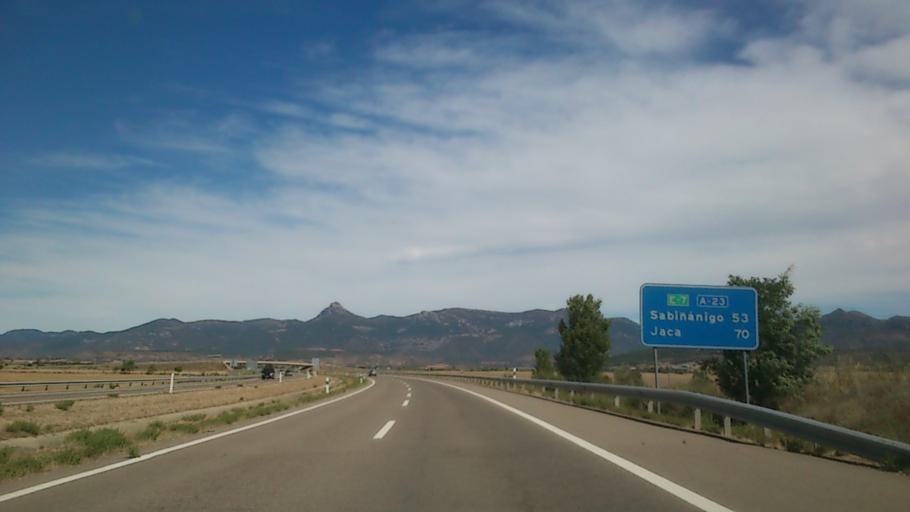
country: ES
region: Aragon
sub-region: Provincia de Huesca
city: Banastas
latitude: 42.1857
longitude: -0.4311
